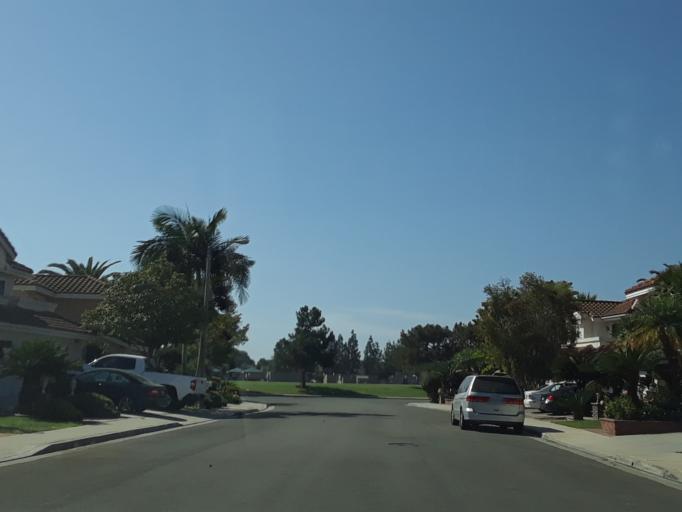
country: US
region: California
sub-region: Orange County
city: Irvine
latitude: 33.6771
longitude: -117.8198
